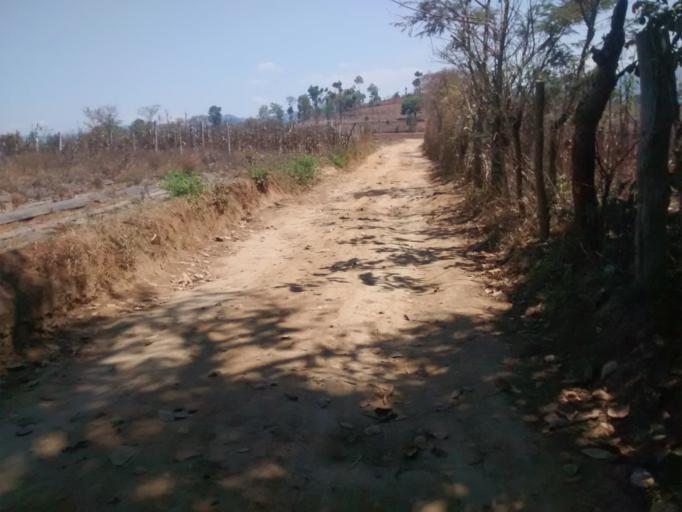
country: GT
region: Sacatepequez
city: Sumpango
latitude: 14.6681
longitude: -90.7339
